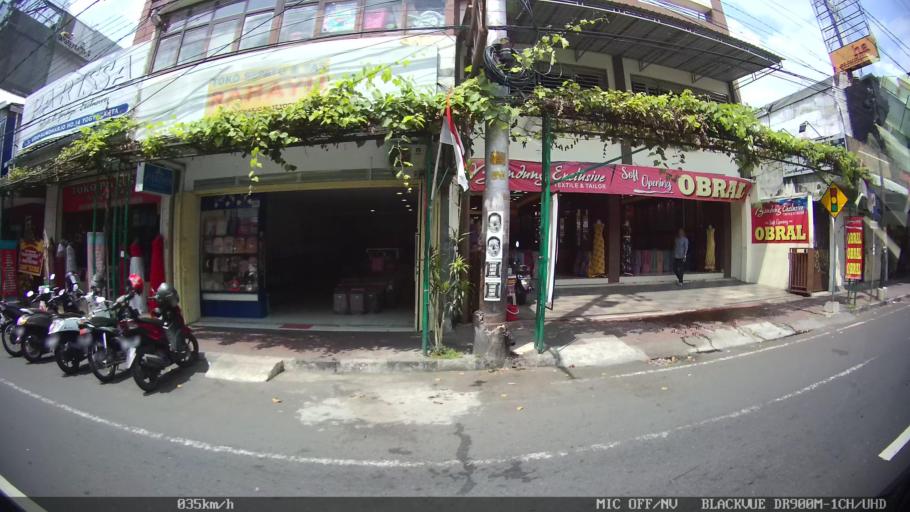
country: ID
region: Daerah Istimewa Yogyakarta
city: Yogyakarta
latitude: -7.7833
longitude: 110.3800
